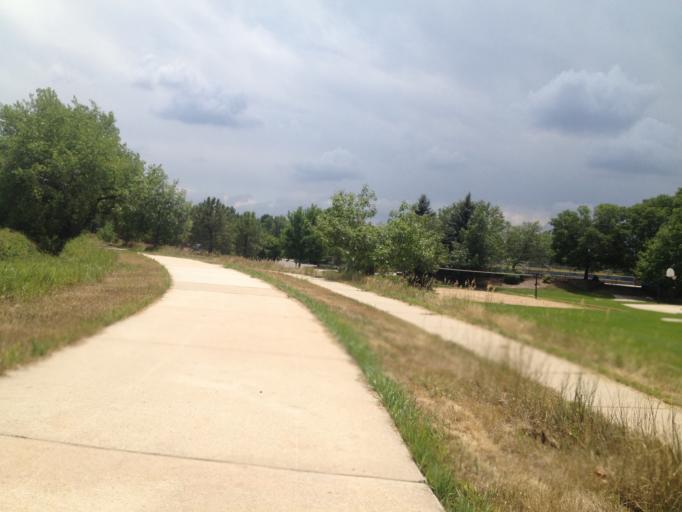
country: US
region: Colorado
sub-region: Boulder County
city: Louisville
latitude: 39.9671
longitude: -105.1501
